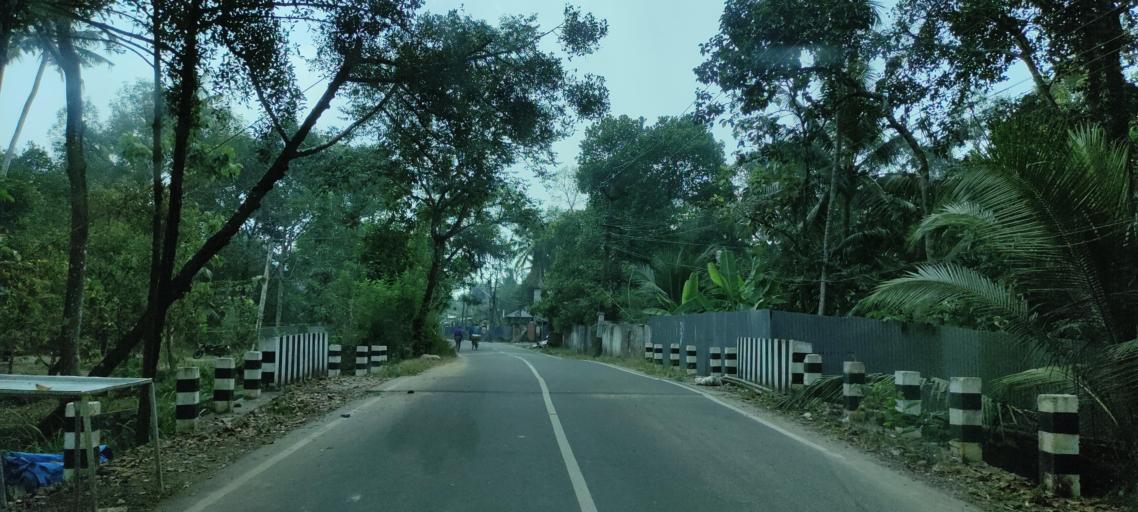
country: IN
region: Kerala
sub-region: Alappuzha
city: Alleppey
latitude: 9.5756
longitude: 76.3395
